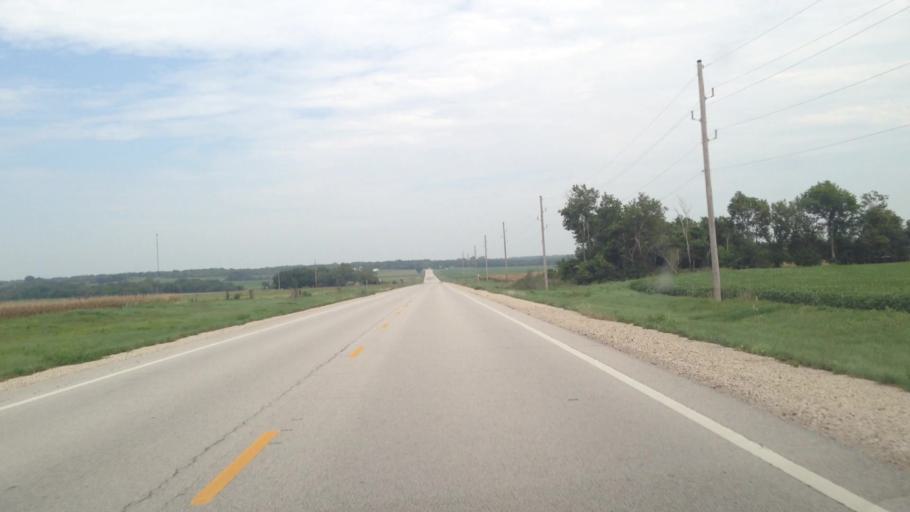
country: US
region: Kansas
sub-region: Anderson County
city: Garnett
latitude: 38.0618
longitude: -95.1693
